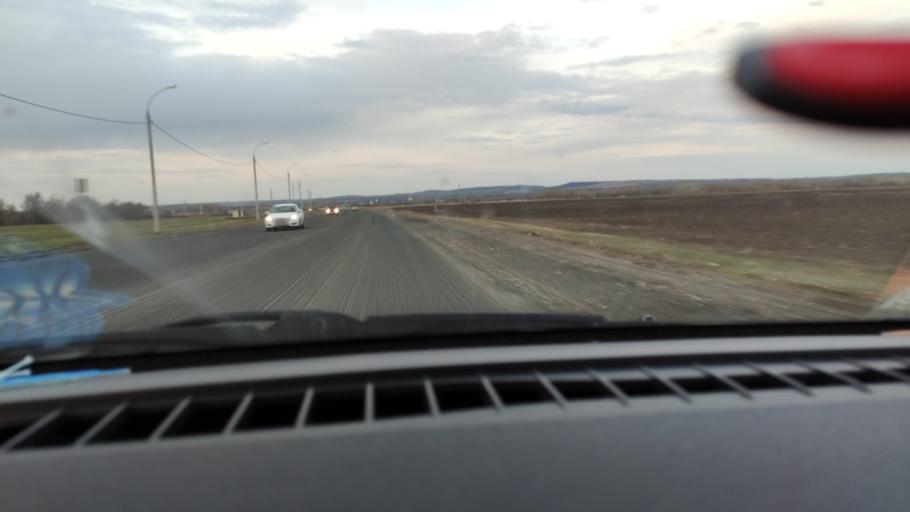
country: RU
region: Saratov
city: Yelshanka
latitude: 51.8162
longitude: 46.2103
